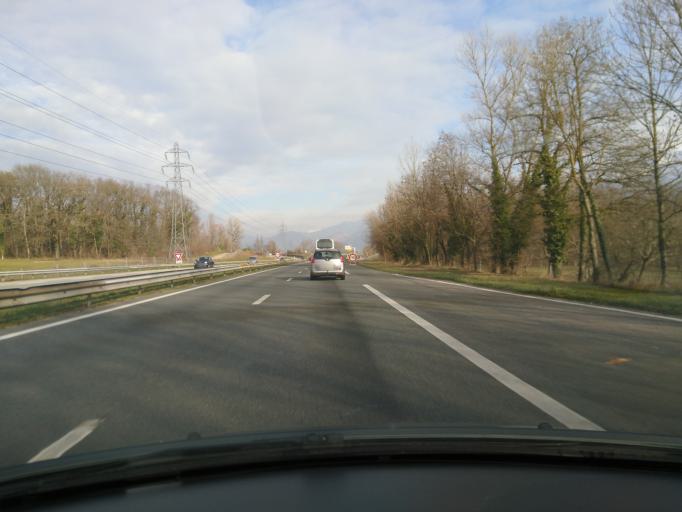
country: FR
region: Rhone-Alpes
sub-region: Departement de l'Isere
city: Saint-Nazaire-les-Eymes
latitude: 45.2377
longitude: 5.8416
